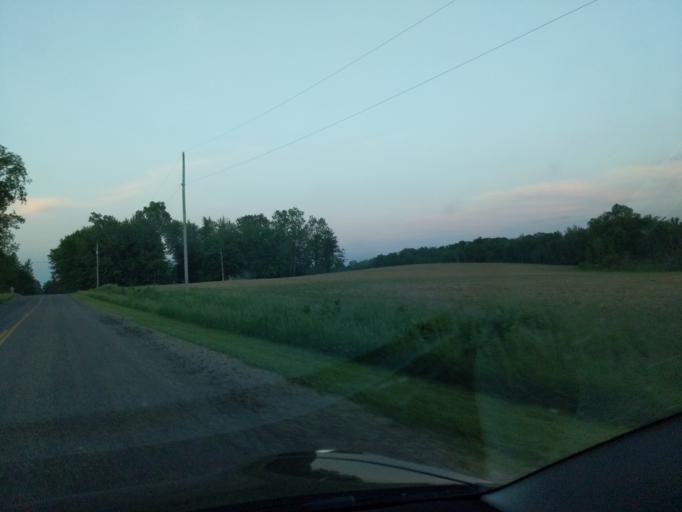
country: US
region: Michigan
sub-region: Barry County
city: Nashville
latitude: 42.5383
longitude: -85.0330
